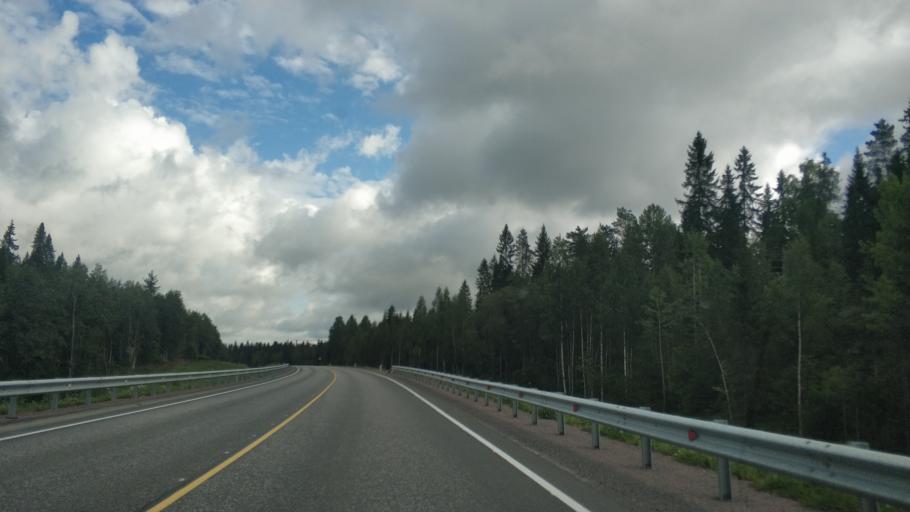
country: RU
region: Republic of Karelia
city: Ruskeala
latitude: 61.8630
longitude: 30.6531
